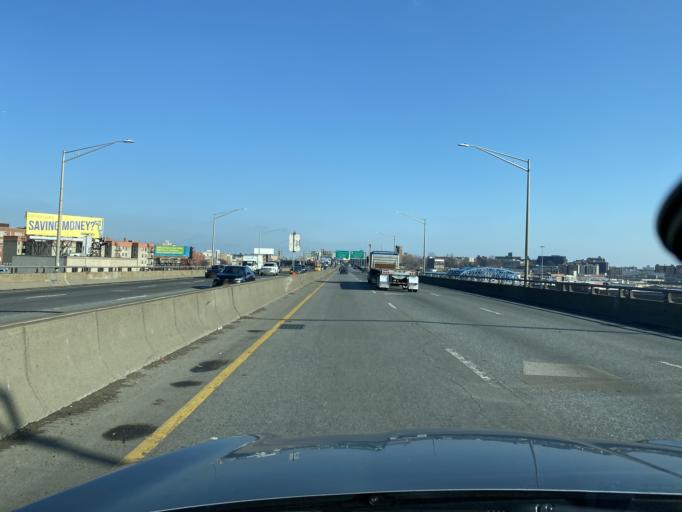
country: US
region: New York
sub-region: Bronx
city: The Bronx
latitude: 40.8108
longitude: -73.9024
